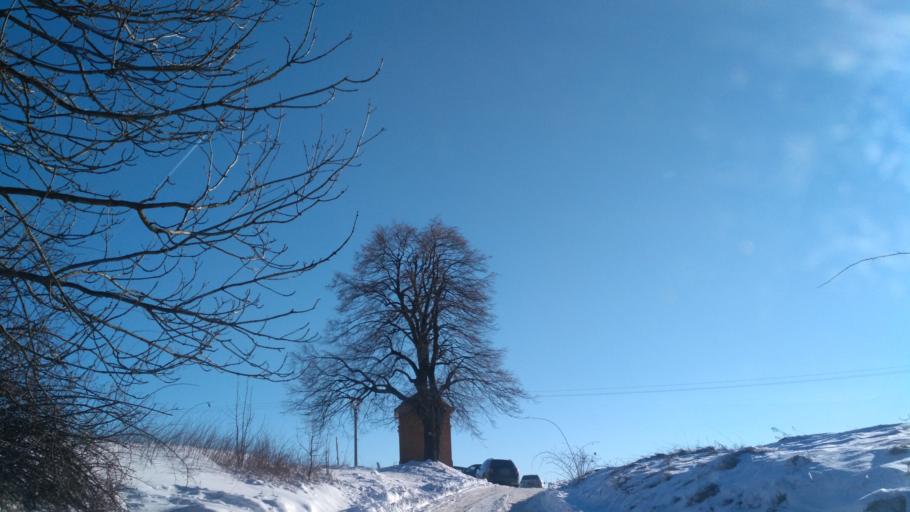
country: SK
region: Kosicky
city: Kosice
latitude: 48.7695
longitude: 21.2055
